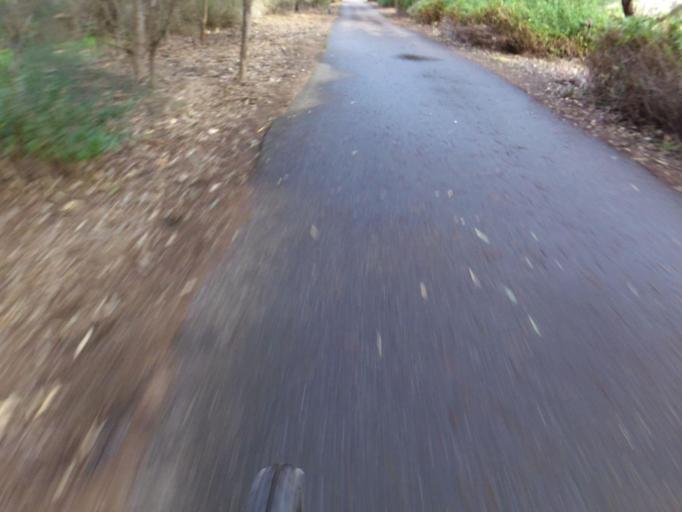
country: AU
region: Victoria
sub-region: Greater Geelong
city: Breakwater
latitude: -38.1761
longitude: 144.3616
